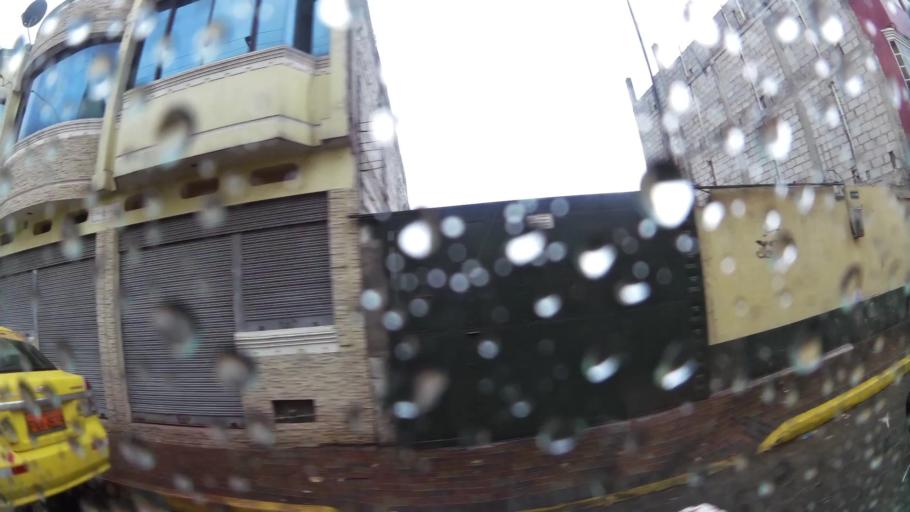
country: EC
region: Pichincha
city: Quito
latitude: -0.3203
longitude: -78.5554
